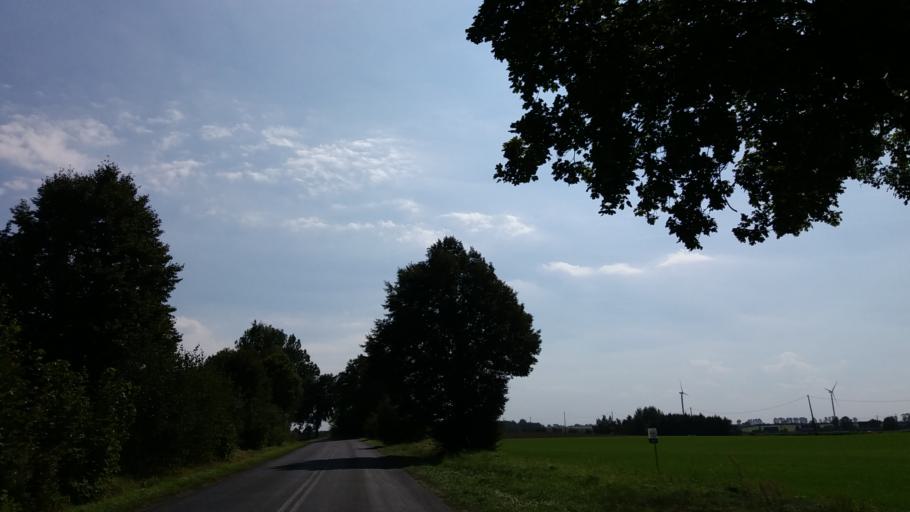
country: PL
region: West Pomeranian Voivodeship
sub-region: Powiat choszczenski
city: Choszczno
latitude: 53.1388
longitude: 15.4525
